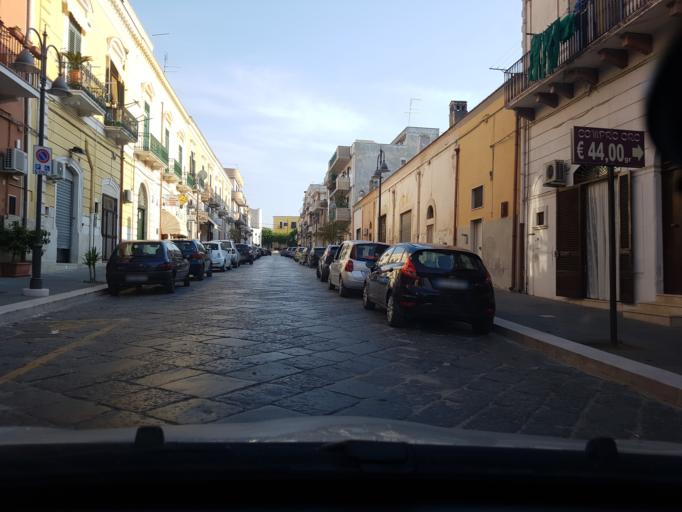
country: IT
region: Apulia
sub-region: Provincia di Foggia
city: Cerignola
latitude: 41.2695
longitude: 15.8944
